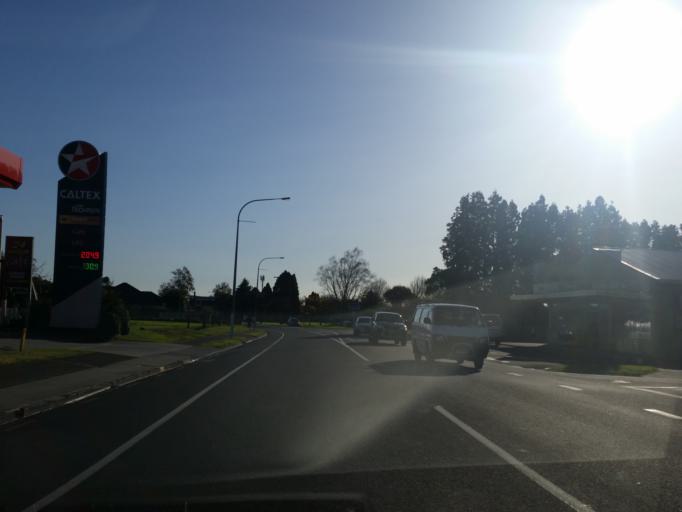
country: NZ
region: Bay of Plenty
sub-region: Western Bay of Plenty District
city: Katikati
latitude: -37.5579
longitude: 175.9164
